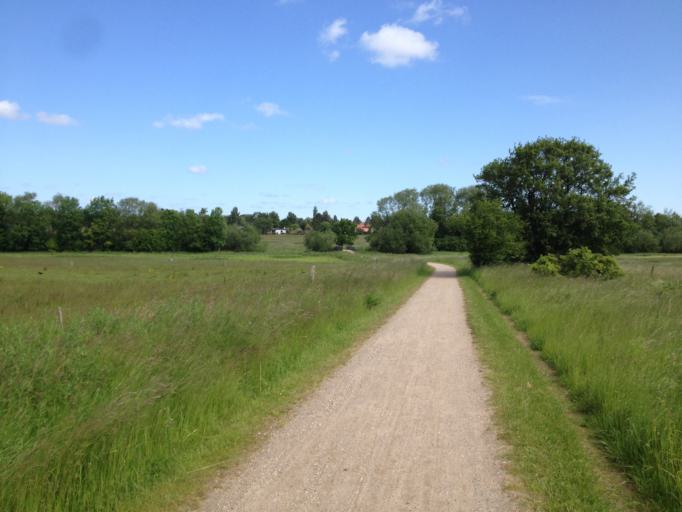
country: DK
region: Capital Region
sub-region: Fredensborg Kommune
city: Niva
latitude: 55.9277
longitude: 12.4901
